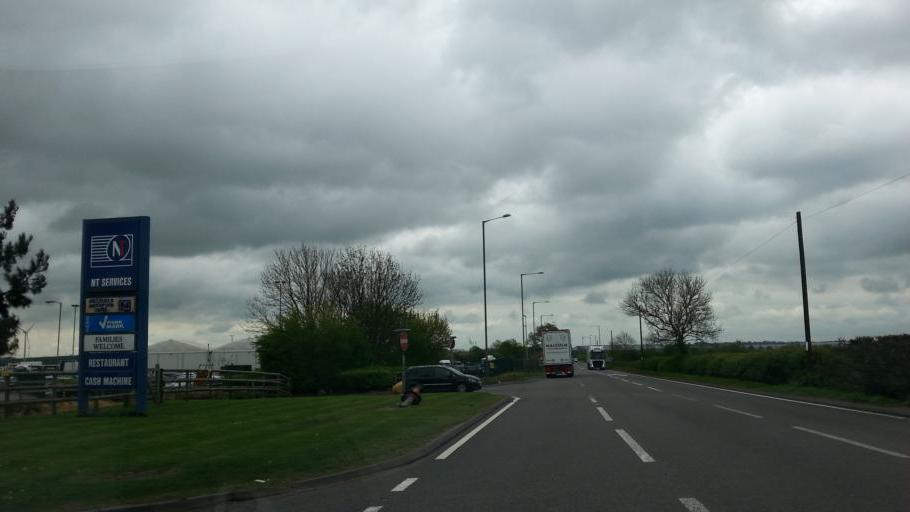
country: GB
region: England
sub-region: Warwickshire
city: Rugby
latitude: 52.3816
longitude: -1.1895
